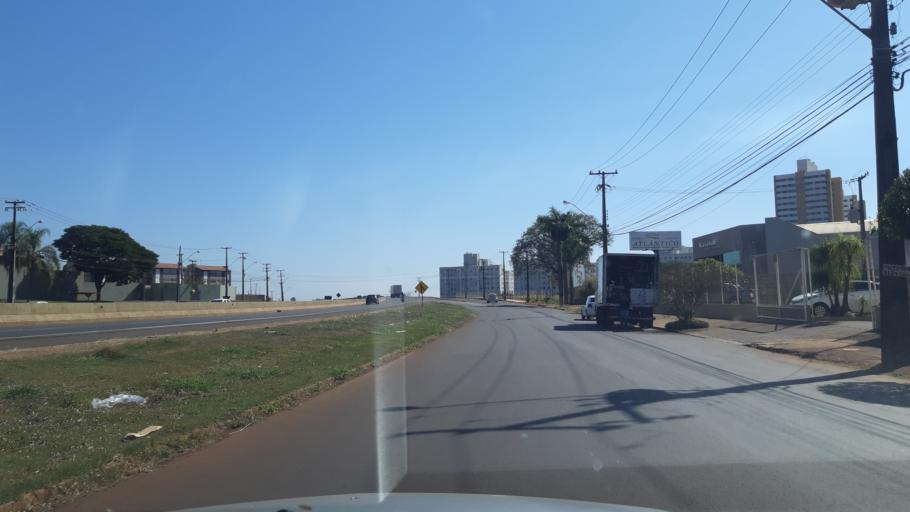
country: BR
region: Parana
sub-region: Londrina
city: Londrina
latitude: -23.3258
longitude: -51.1904
